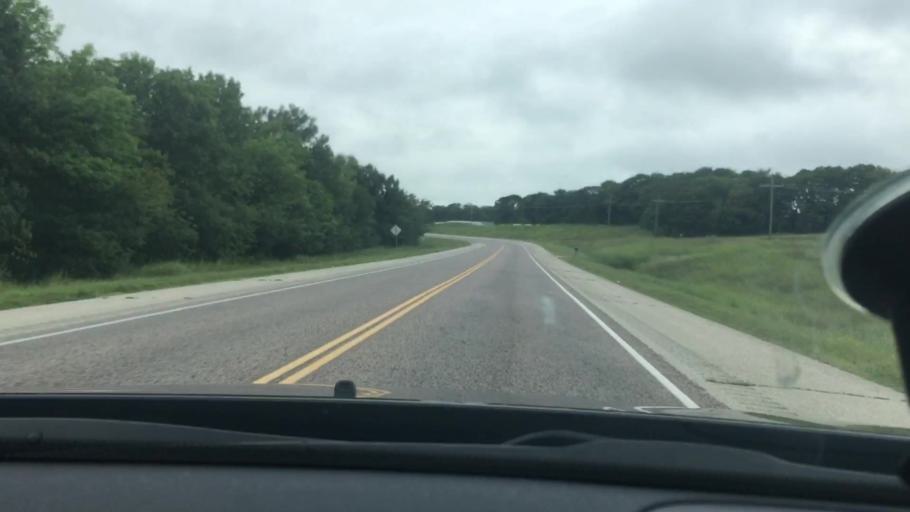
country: US
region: Oklahoma
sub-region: Pontotoc County
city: Ada
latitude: 34.7875
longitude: -96.5682
